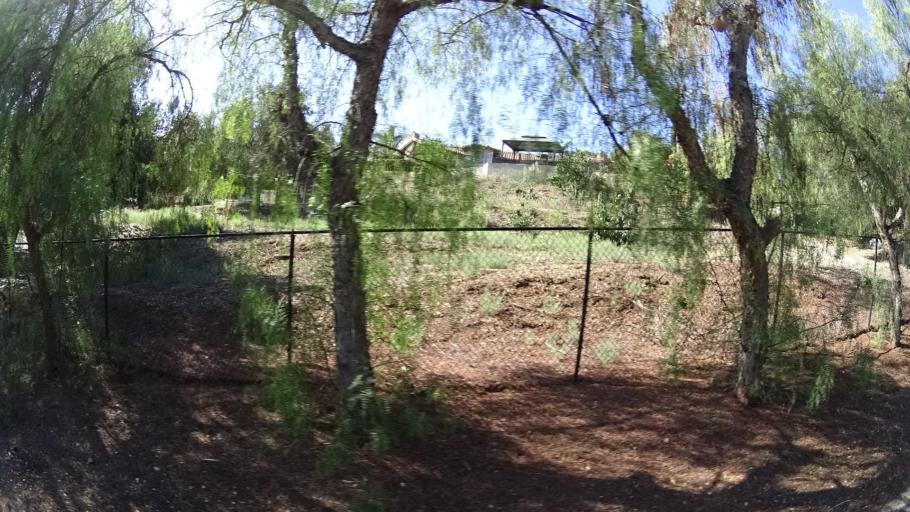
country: US
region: California
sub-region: San Diego County
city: Hidden Meadows
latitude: 33.2332
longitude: -117.1185
